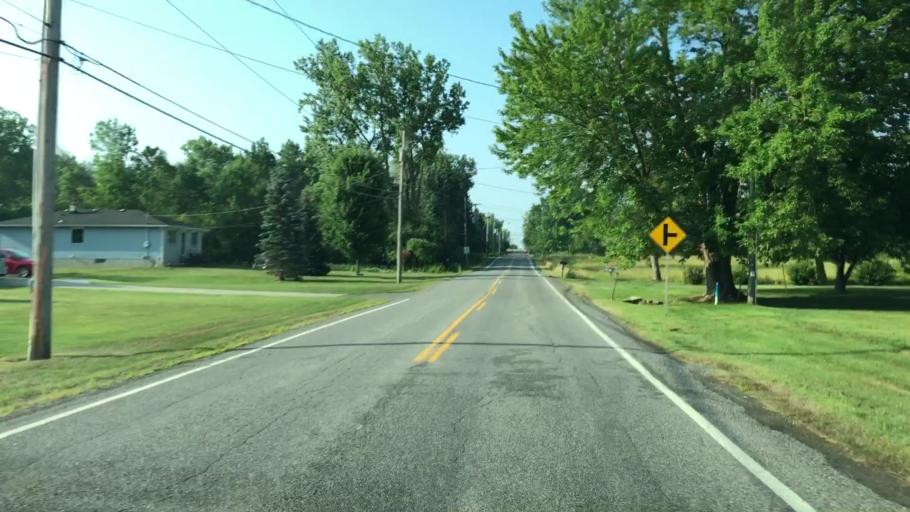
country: US
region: New York
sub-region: Erie County
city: Depew
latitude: 42.8481
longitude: -78.6923
